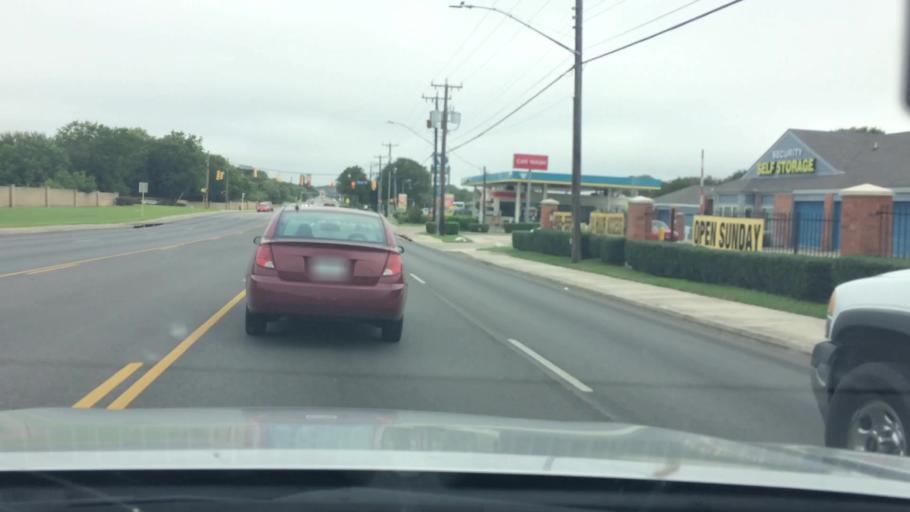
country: US
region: Texas
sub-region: Bexar County
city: Hollywood Park
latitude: 29.5681
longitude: -98.4305
